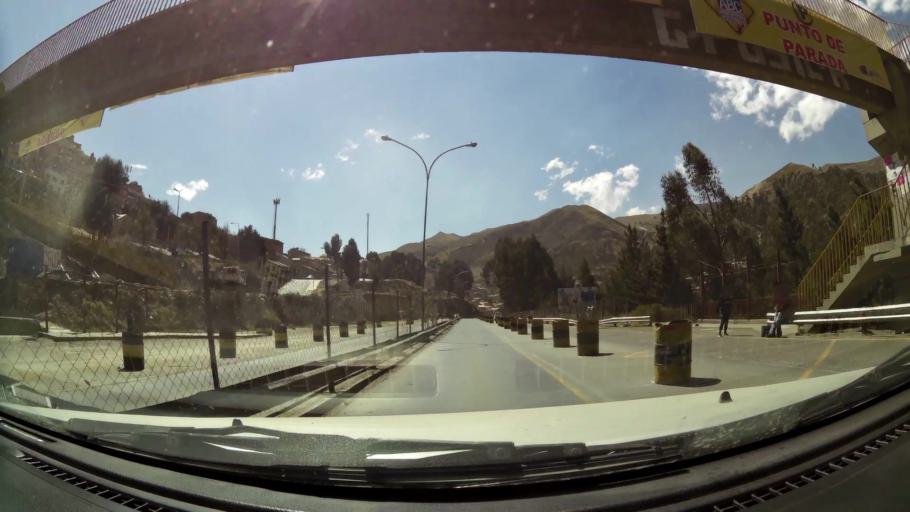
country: BO
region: La Paz
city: La Paz
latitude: -16.4616
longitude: -68.1500
